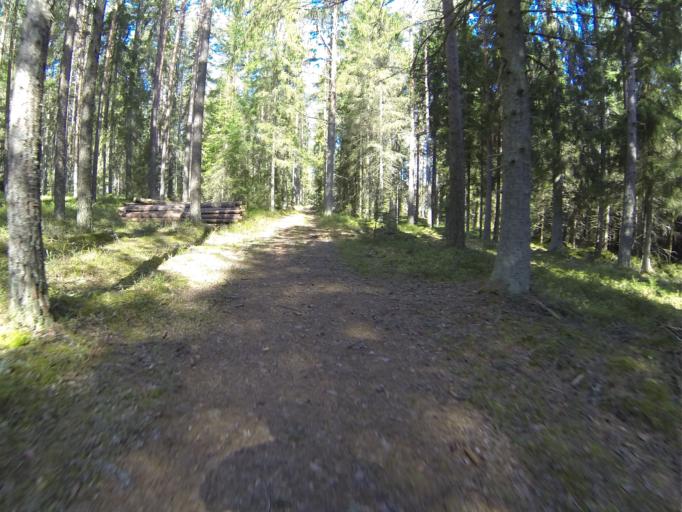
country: FI
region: Varsinais-Suomi
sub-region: Salo
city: Pertteli
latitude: 60.3927
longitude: 23.2192
